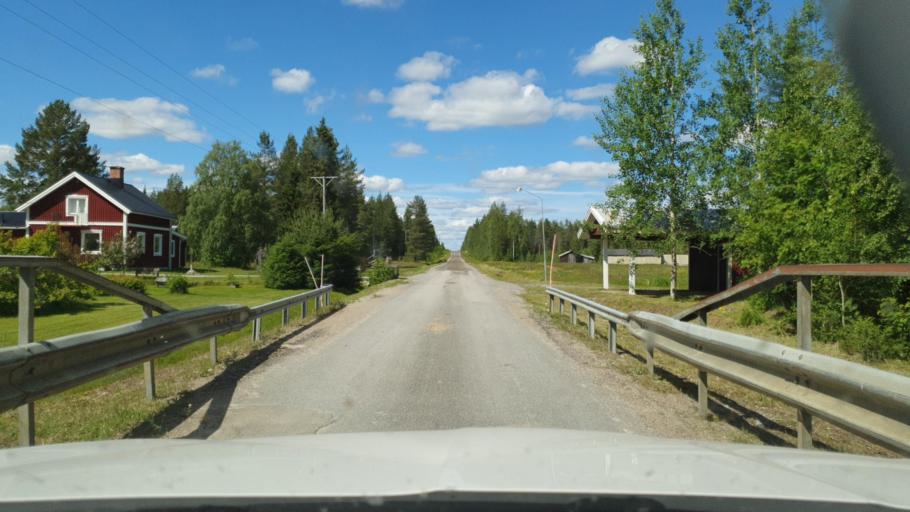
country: SE
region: Vaesterbotten
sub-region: Skelleftea Kommun
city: Backa
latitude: 65.1670
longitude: 21.1259
